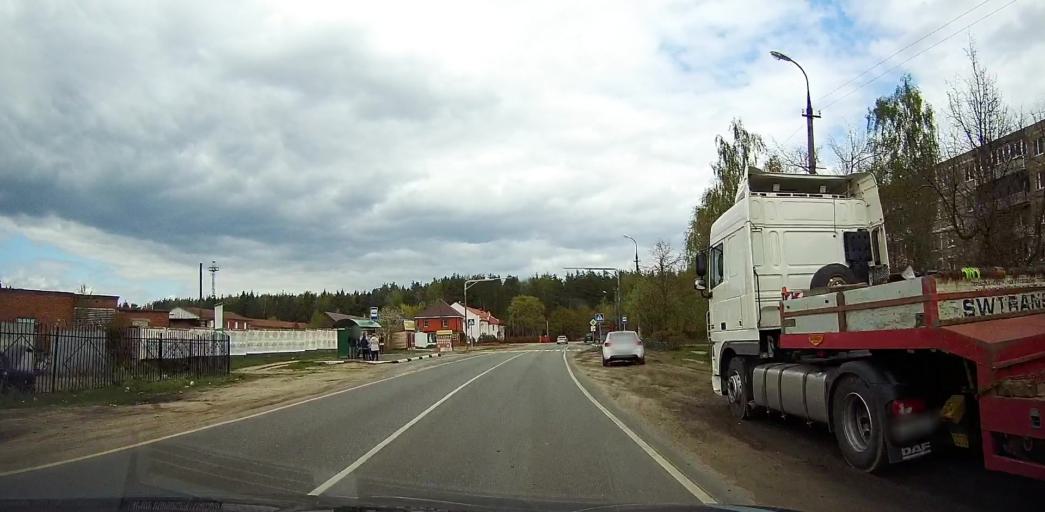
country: RU
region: Moskovskaya
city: Ashitkovo
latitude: 55.4374
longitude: 38.5793
